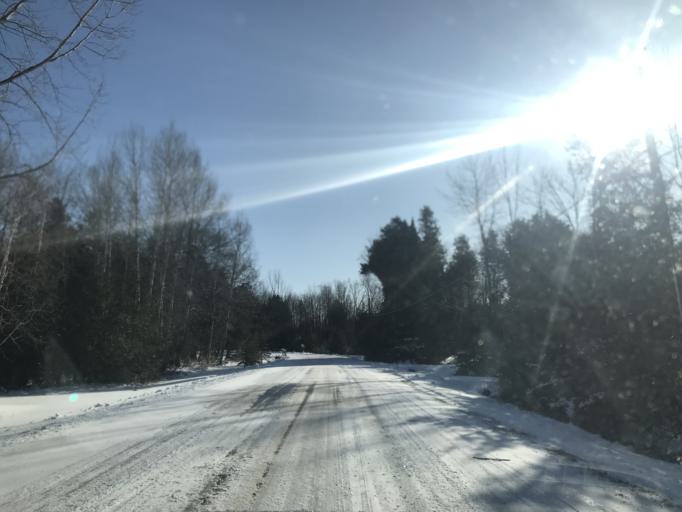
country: US
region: Wisconsin
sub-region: Door County
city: Sturgeon Bay
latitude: 44.8468
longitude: -87.5099
